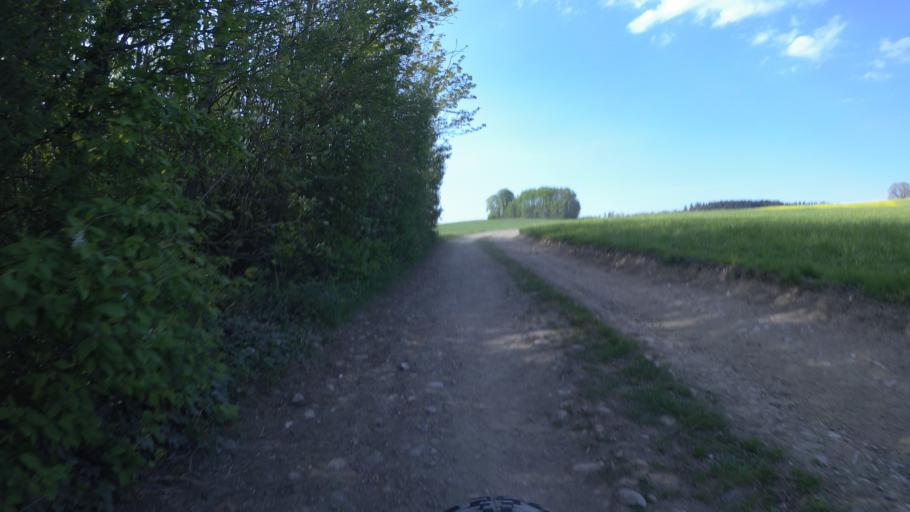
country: DE
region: Bavaria
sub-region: Upper Bavaria
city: Chieming
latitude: 47.9068
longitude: 12.5188
